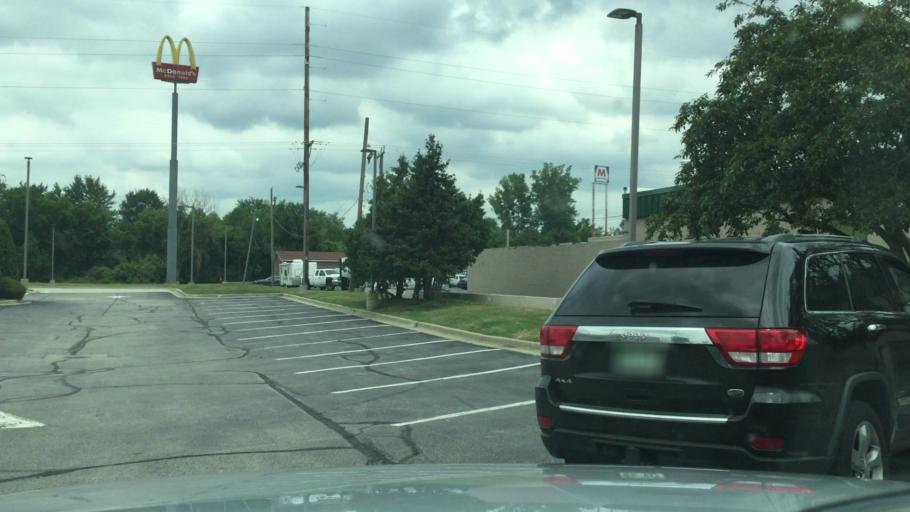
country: US
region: Michigan
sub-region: Saginaw County
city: Birch Run
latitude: 43.2504
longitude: -83.7798
